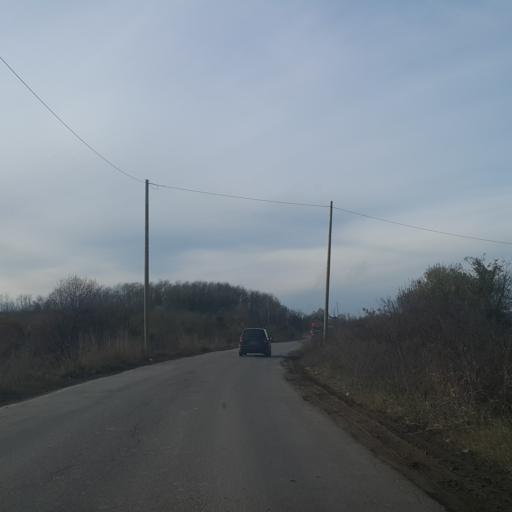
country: RS
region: Central Serbia
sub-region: Belgrade
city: Lazarevac
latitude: 44.4020
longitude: 20.3546
